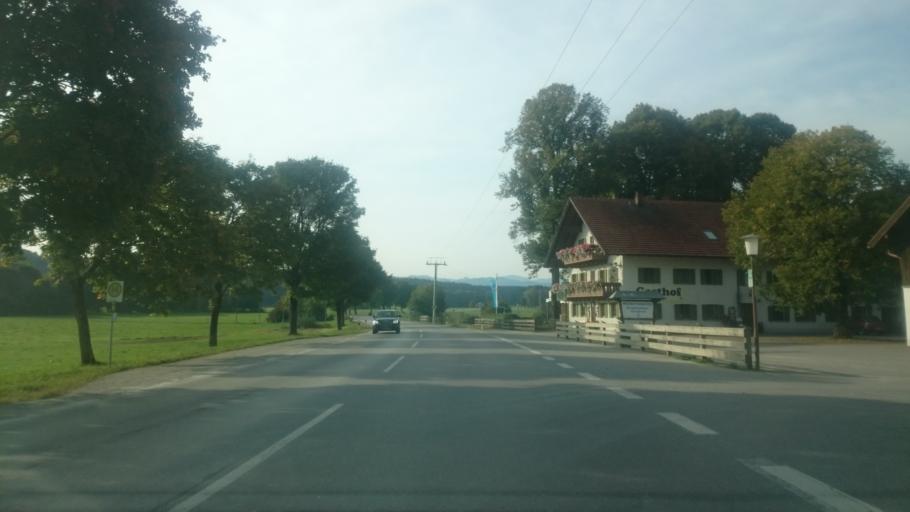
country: DE
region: Bavaria
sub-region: Upper Bavaria
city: Peiting
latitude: 47.7663
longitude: 10.9024
